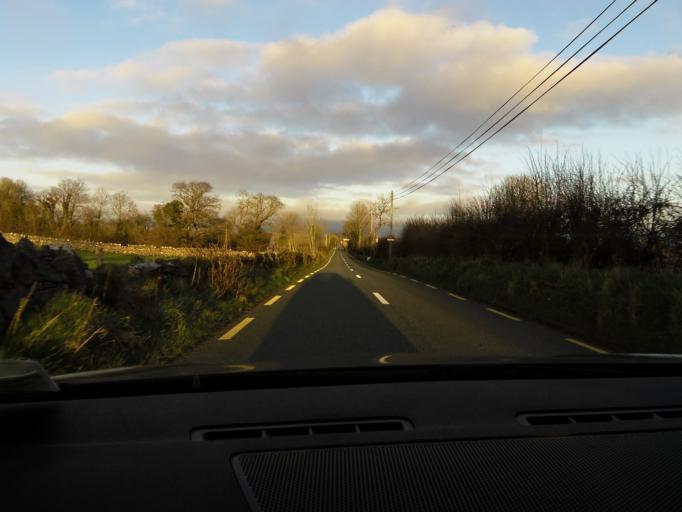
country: IE
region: Connaught
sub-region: Sligo
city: Tobercurry
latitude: 54.0440
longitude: -8.6663
